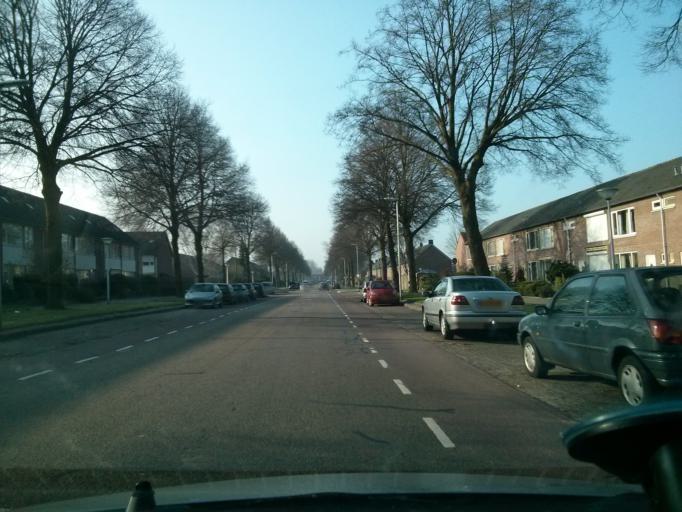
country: NL
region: North Brabant
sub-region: Gemeente Son en Breugel
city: Son
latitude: 51.4812
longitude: 5.5010
